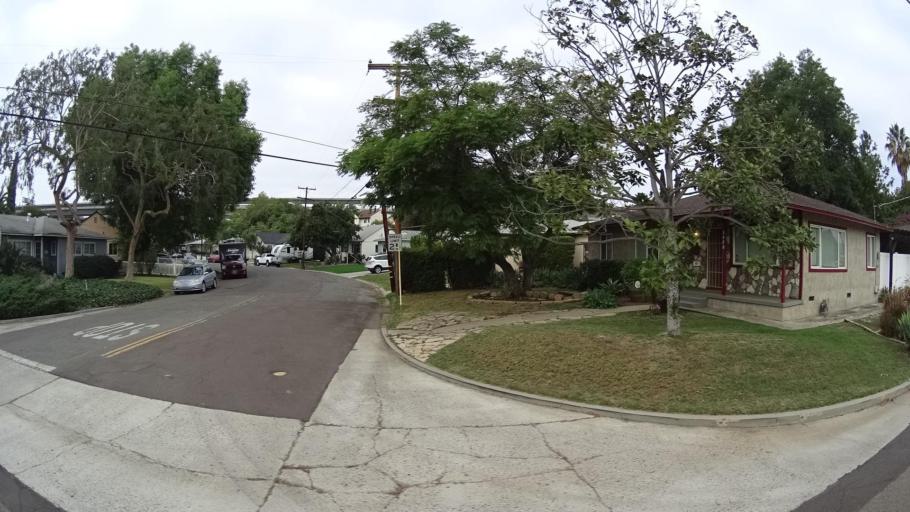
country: US
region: California
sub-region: San Diego County
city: Spring Valley
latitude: 32.7465
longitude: -117.0151
